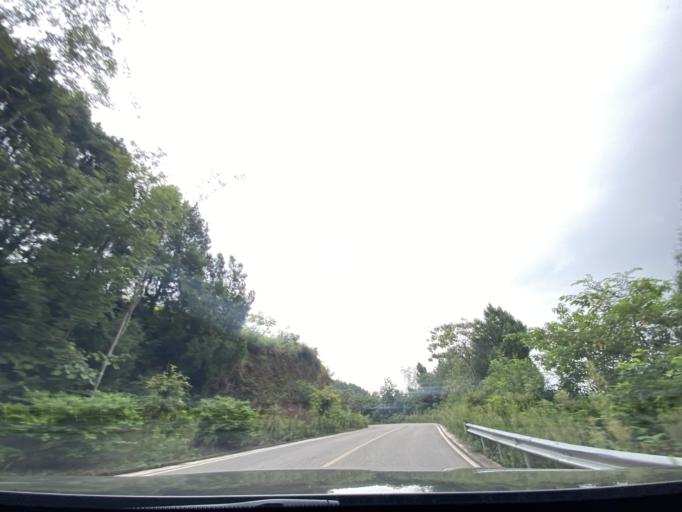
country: CN
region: Sichuan
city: Jiancheng
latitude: 30.5354
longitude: 104.5322
